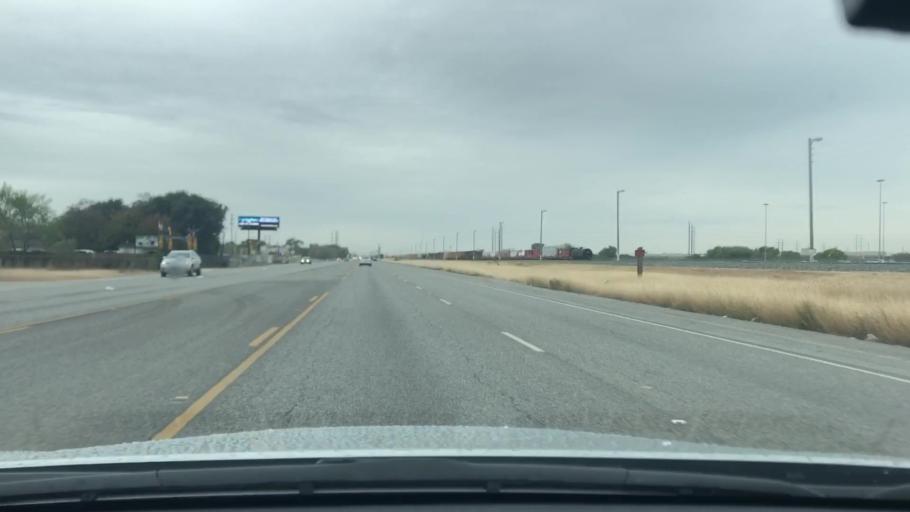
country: US
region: Texas
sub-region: Bexar County
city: Kirby
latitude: 29.4724
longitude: -98.3852
